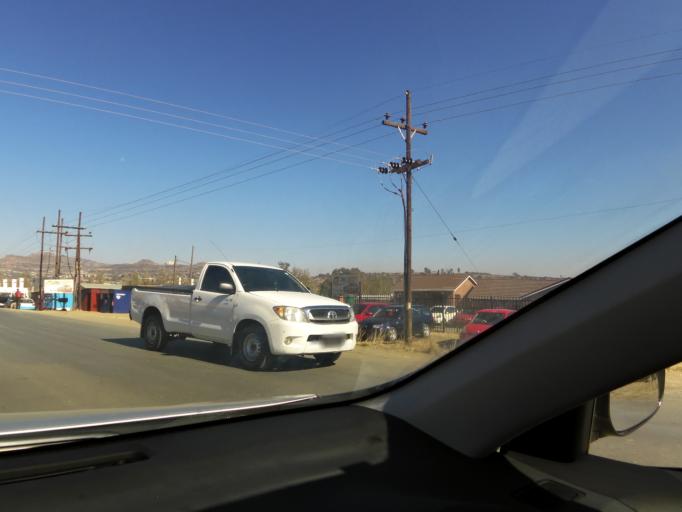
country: LS
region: Maseru
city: Maseru
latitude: -29.3009
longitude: 27.5170
